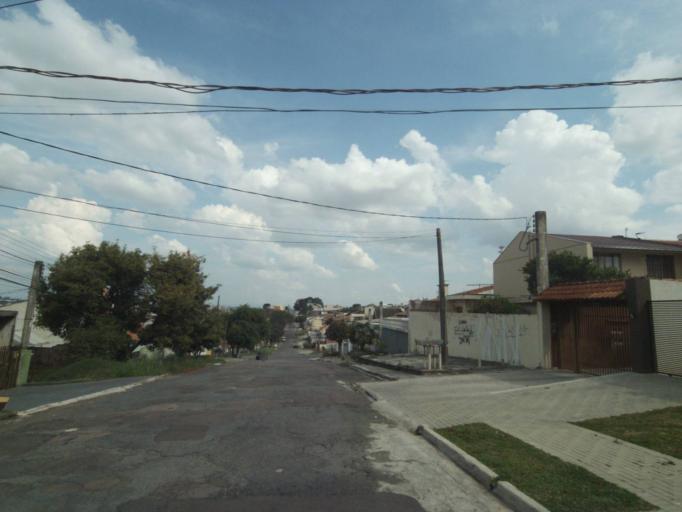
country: BR
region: Parana
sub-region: Pinhais
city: Pinhais
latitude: -25.4122
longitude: -49.2078
